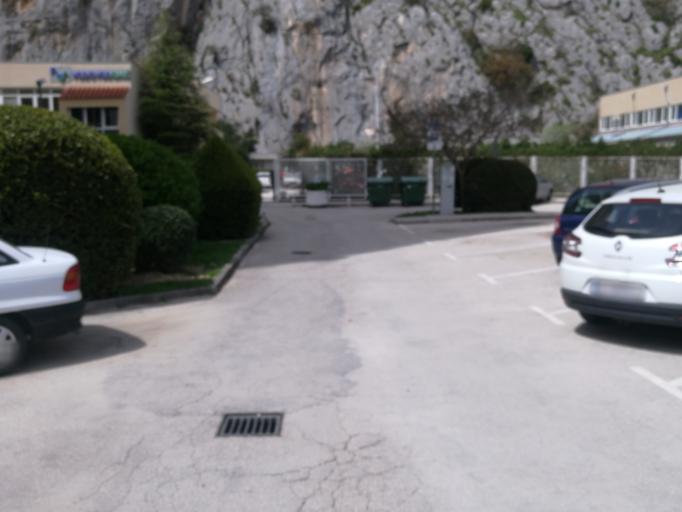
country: HR
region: Splitsko-Dalmatinska
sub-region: Grad Omis
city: Omis
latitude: 43.4456
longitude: 16.6867
